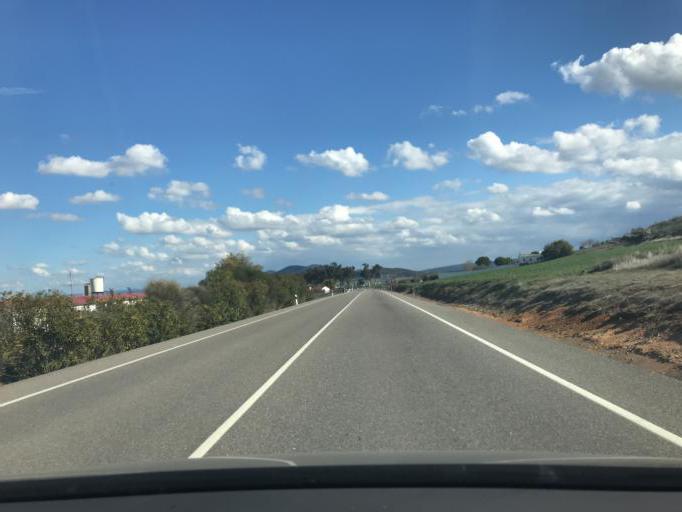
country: ES
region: Andalusia
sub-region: Province of Cordoba
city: Fuente Obejuna
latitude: 38.2754
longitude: -5.4156
